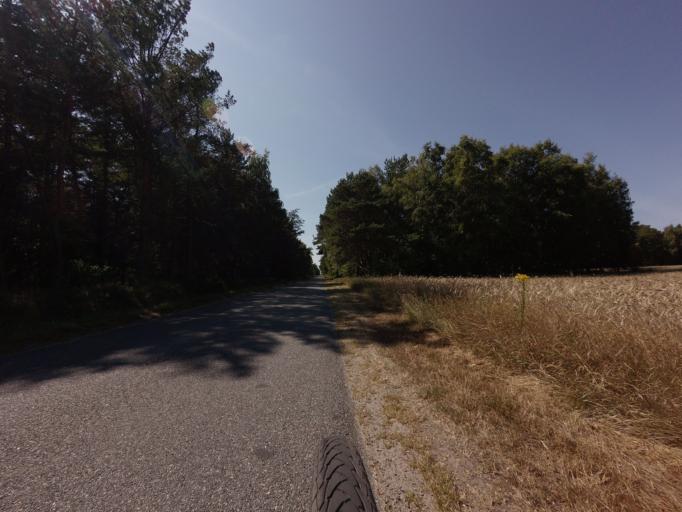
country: DK
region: North Denmark
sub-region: Laeso Kommune
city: Byrum
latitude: 57.2927
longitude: 10.9494
